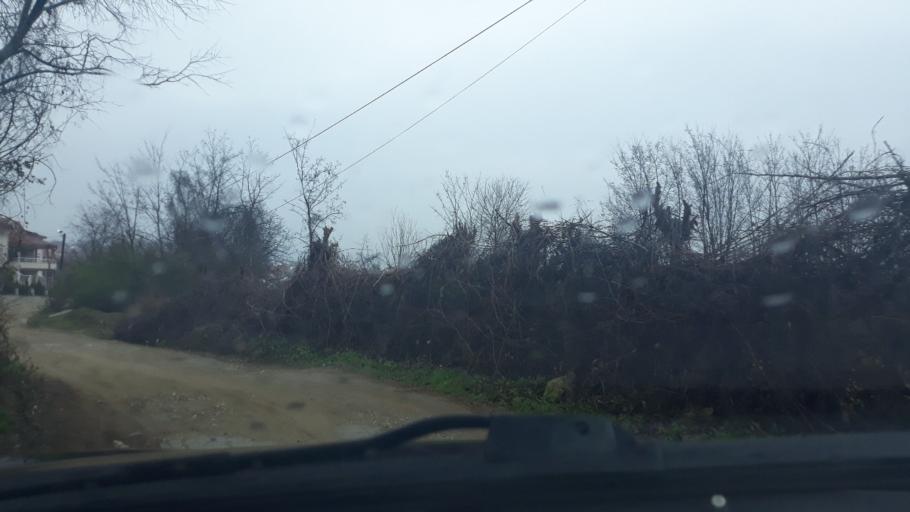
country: MK
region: Valandovo
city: Valandovo
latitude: 41.3170
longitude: 22.5504
